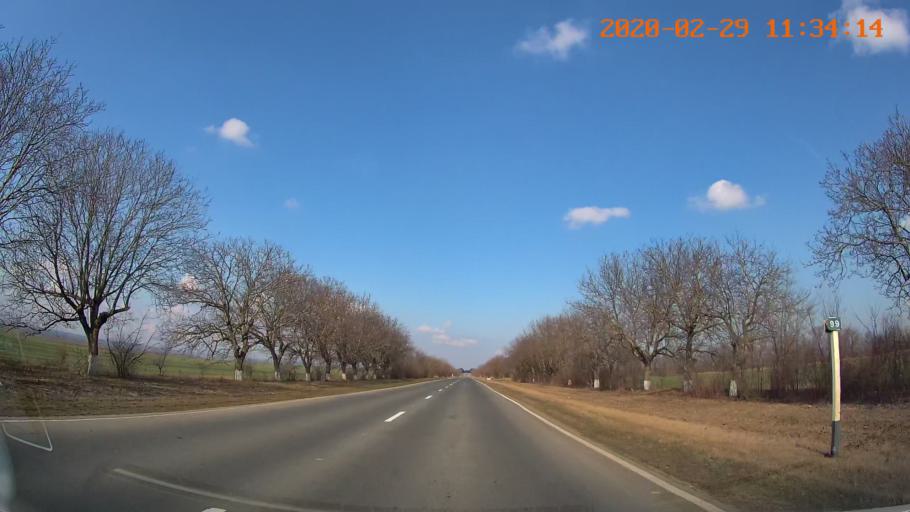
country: MD
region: Rezina
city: Saharna
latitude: 47.5627
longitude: 29.0761
